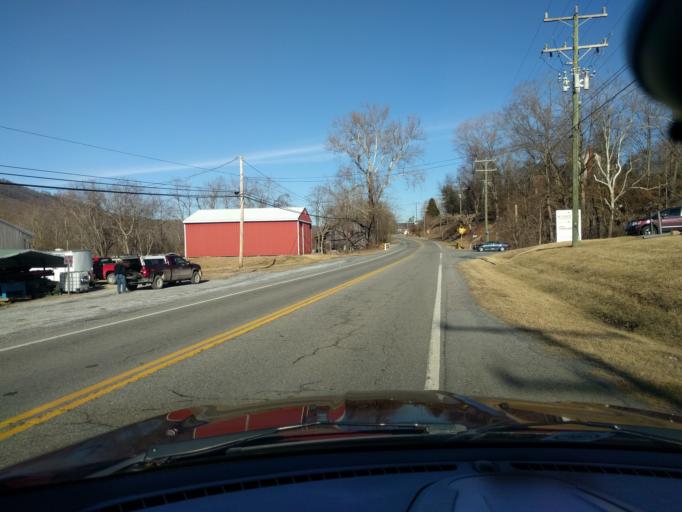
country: US
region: Virginia
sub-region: Botetourt County
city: Buchanan
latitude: 37.5209
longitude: -79.6889
